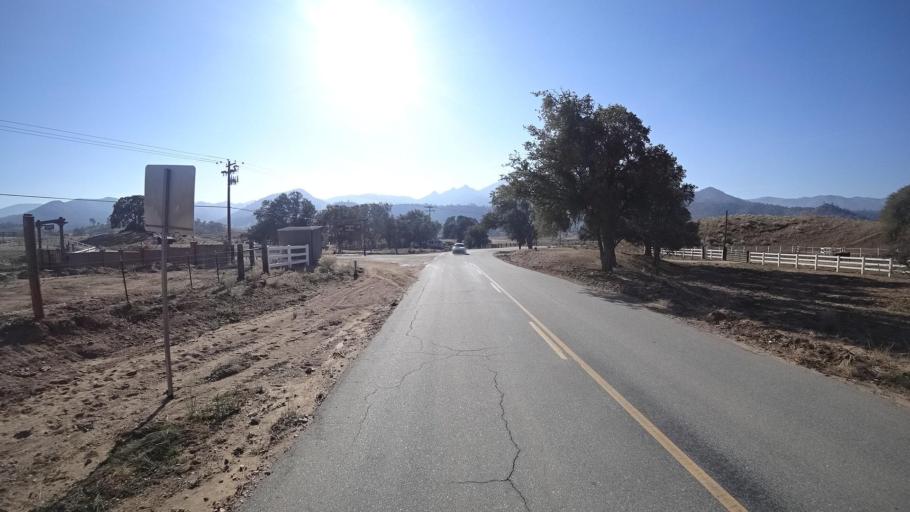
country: US
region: California
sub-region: Kern County
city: Tehachapi
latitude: 35.3231
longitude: -118.3906
